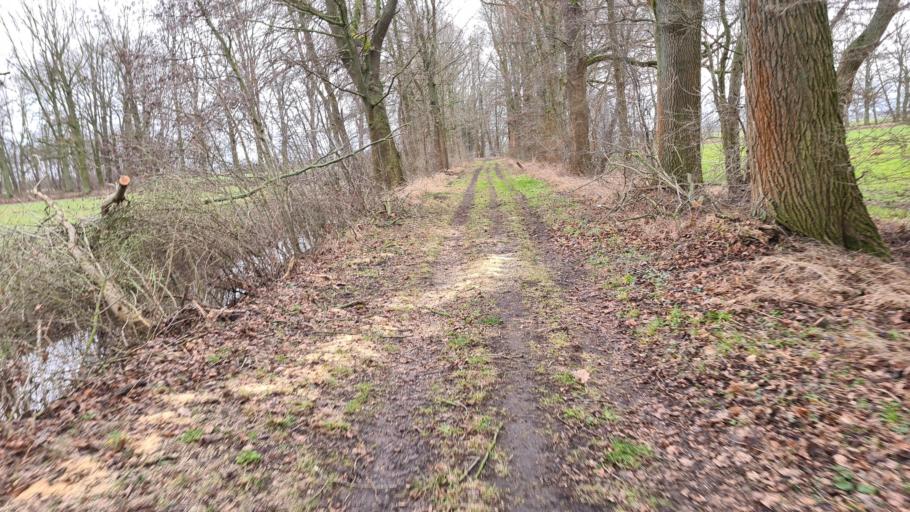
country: DE
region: Brandenburg
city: Schonewalde
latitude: 51.6951
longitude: 13.5984
